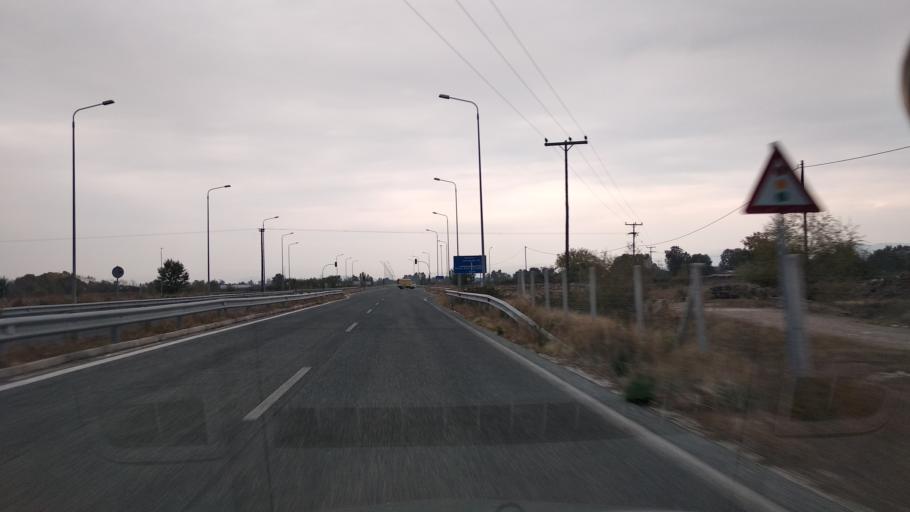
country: GR
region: Thessaly
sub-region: Trikala
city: Pyrgetos
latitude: 39.5481
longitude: 21.7349
